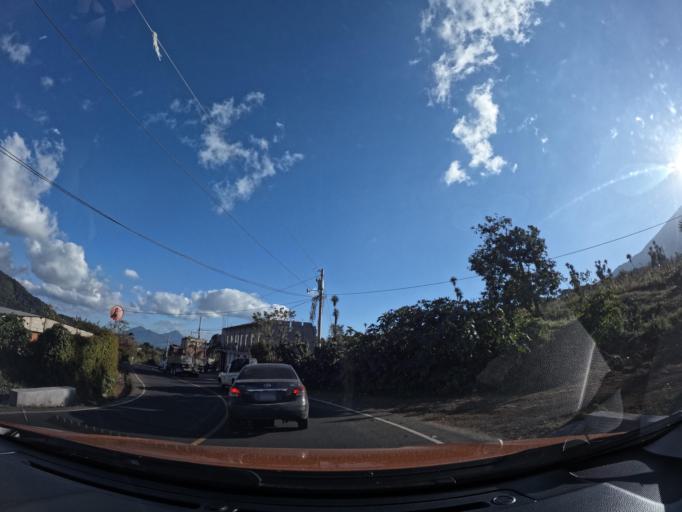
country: GT
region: Sacatepequez
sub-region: Municipio de Santa Maria de Jesus
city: Santa Maria de Jesus
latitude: 14.4866
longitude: -90.7060
